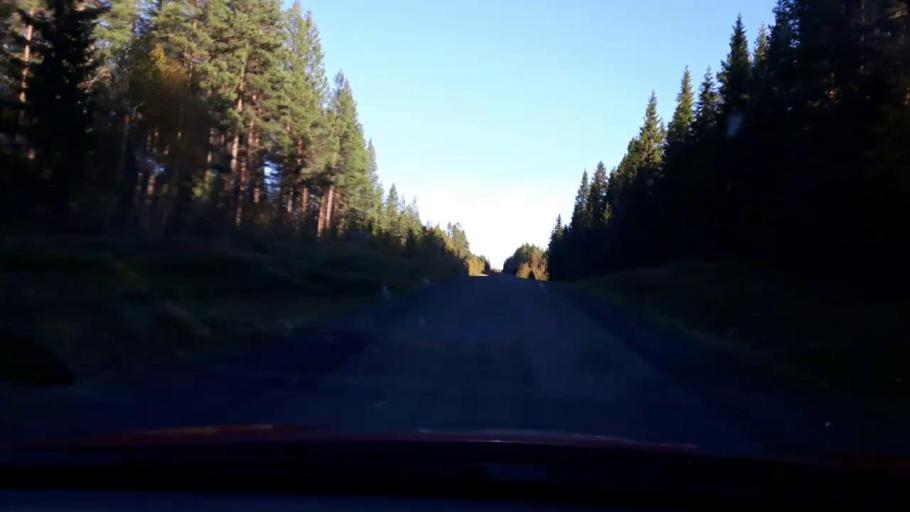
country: SE
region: Jaemtland
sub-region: OEstersunds Kommun
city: Lit
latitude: 63.6012
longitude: 14.8086
